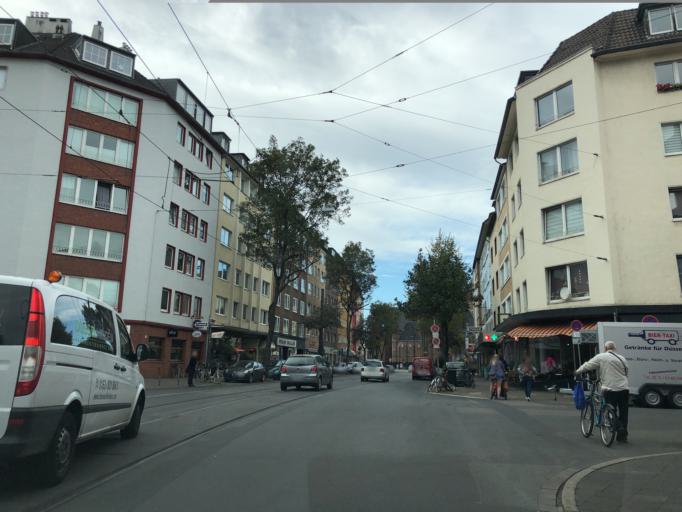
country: DE
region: North Rhine-Westphalia
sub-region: Regierungsbezirk Dusseldorf
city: Dusseldorf
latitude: 51.2109
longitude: 6.7671
